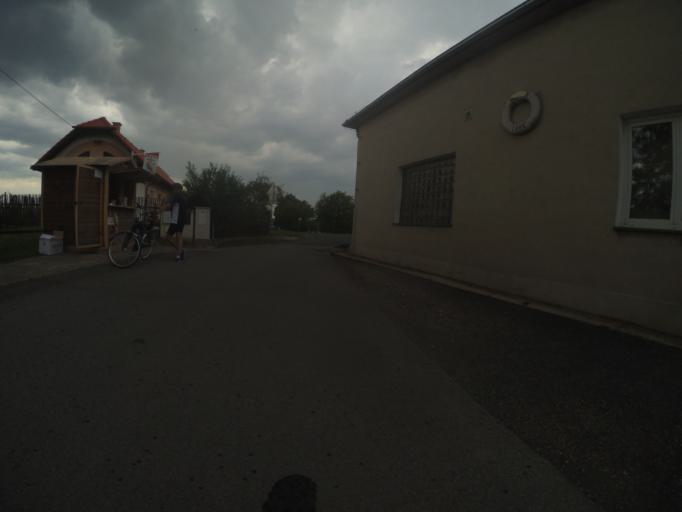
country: CZ
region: Central Bohemia
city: Dolni Berkovice
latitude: 50.4002
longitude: 14.4468
